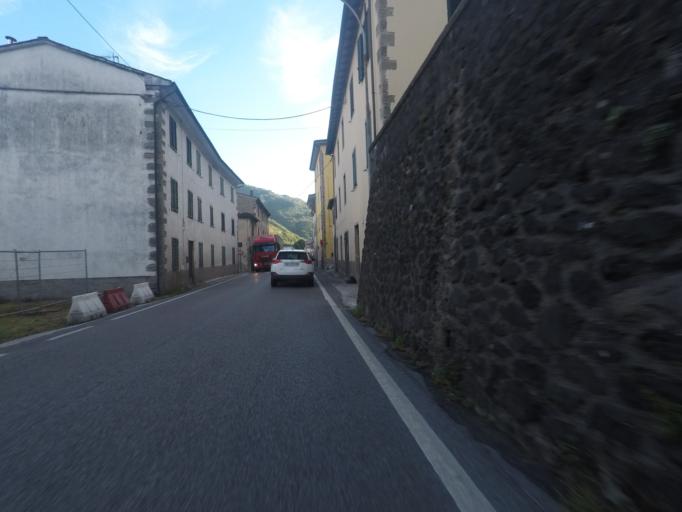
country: IT
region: Tuscany
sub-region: Provincia di Lucca
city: Bagni di Lucca
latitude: 44.0038
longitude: 10.5621
